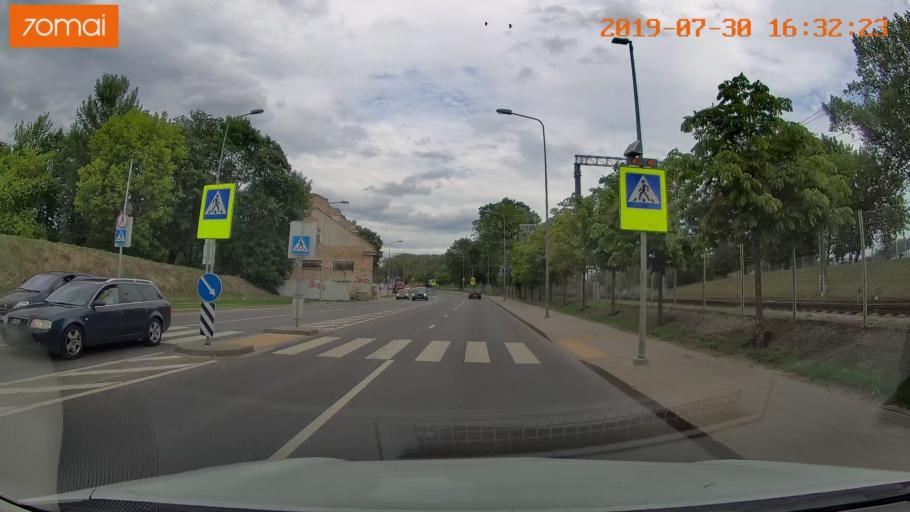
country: LT
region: Vilnius County
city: Rasos
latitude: 54.6725
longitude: 25.2934
